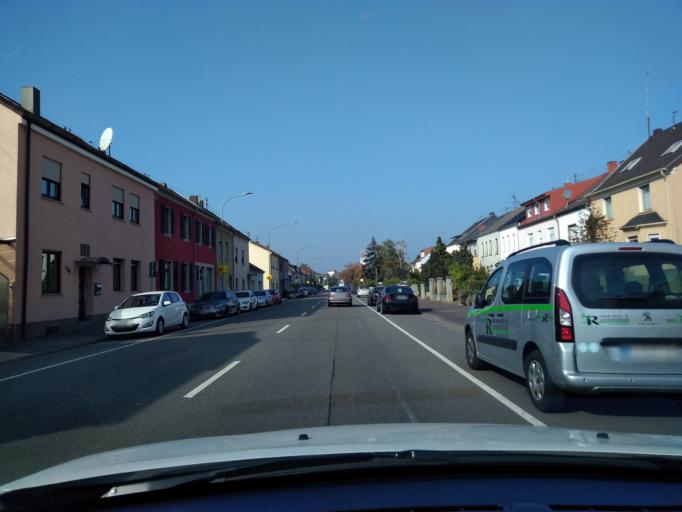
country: DE
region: Saarland
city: Saarlouis
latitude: 49.3222
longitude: 6.7717
